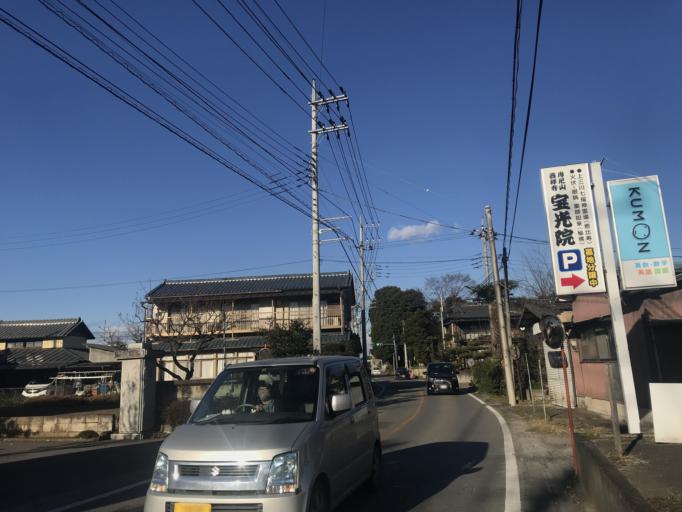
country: JP
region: Tochigi
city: Kaminokawa
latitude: 36.4300
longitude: 139.8714
